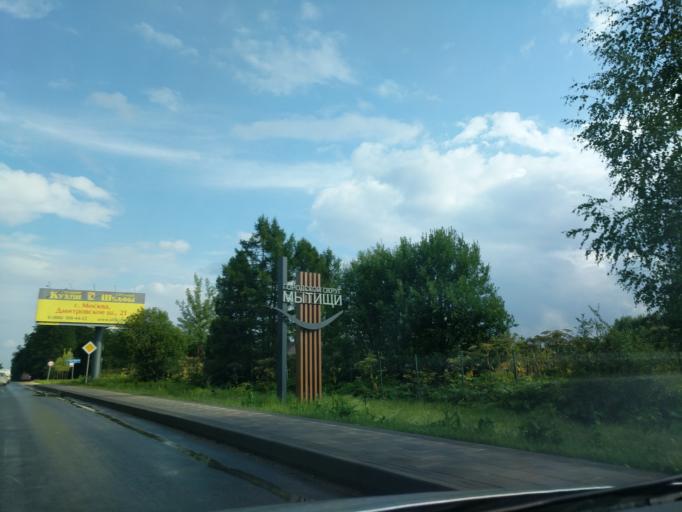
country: RU
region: Moskovskaya
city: Lobnya
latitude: 56.0088
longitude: 37.5091
